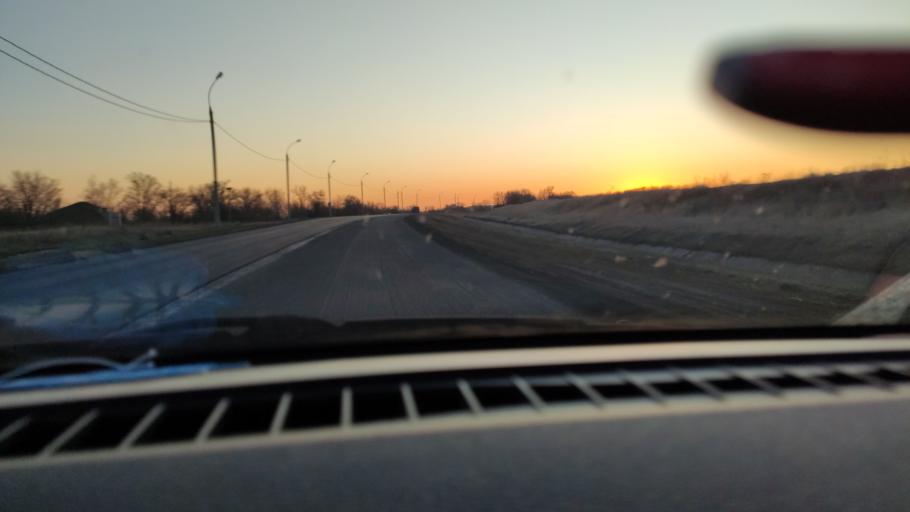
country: RU
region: Saratov
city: Yelshanka
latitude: 51.8281
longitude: 46.2246
